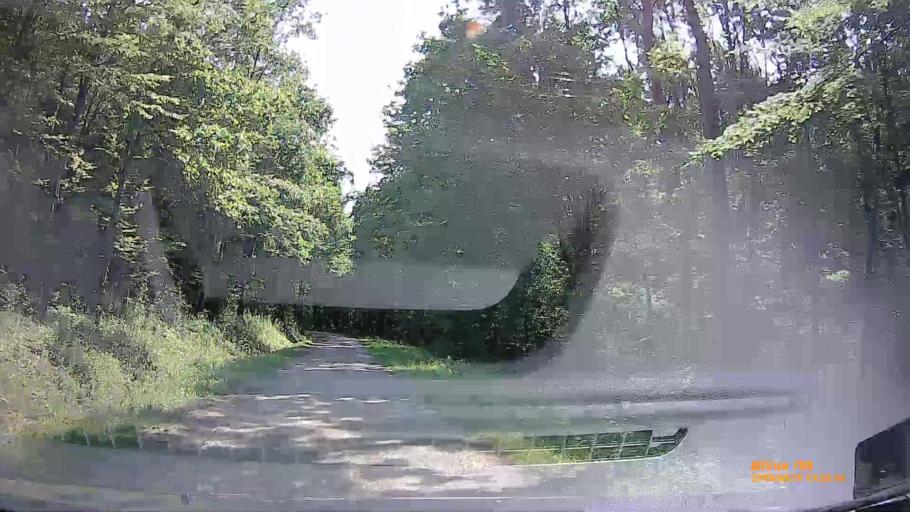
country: HU
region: Baranya
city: Buekkoesd
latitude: 46.1332
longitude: 17.9902
